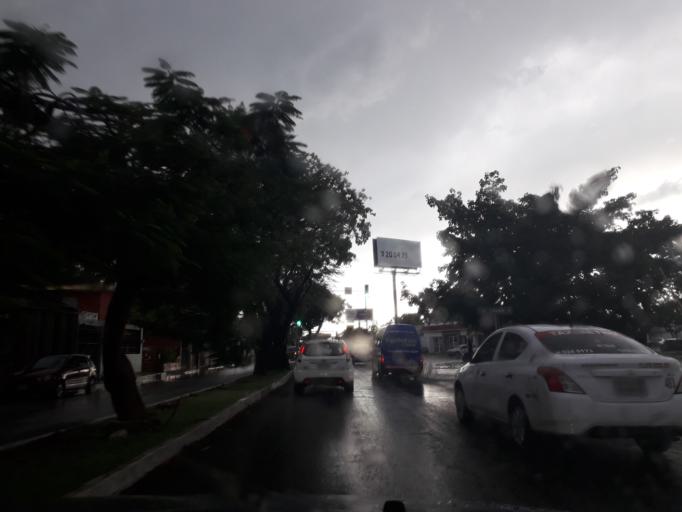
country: MX
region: Yucatan
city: Merida
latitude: 20.9783
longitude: -89.6453
